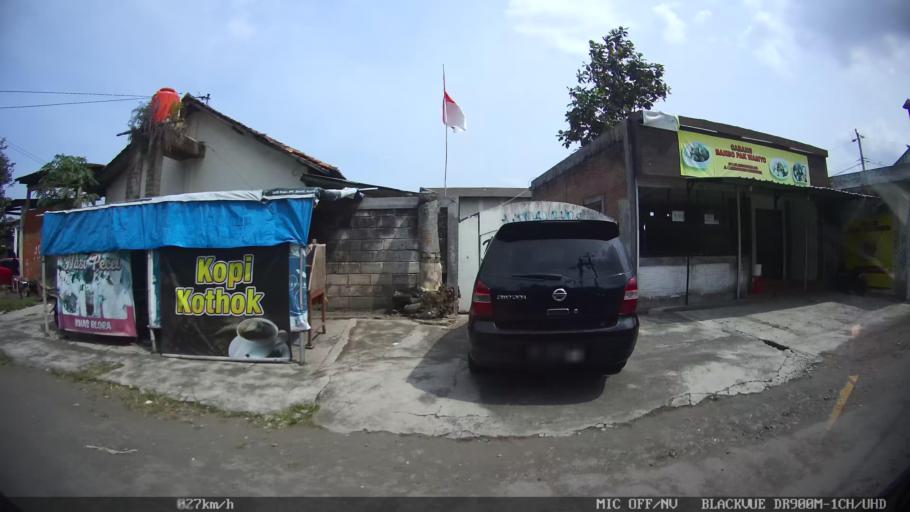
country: ID
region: Daerah Istimewa Yogyakarta
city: Depok
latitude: -7.7849
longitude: 110.4046
